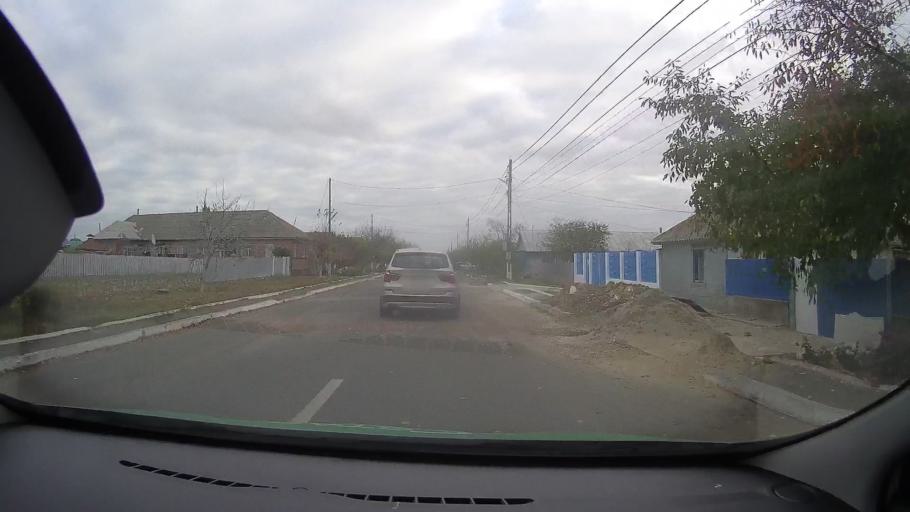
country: RO
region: Tulcea
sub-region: Comuna Jurilovca
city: Jurilovca
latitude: 44.7600
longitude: 28.8809
